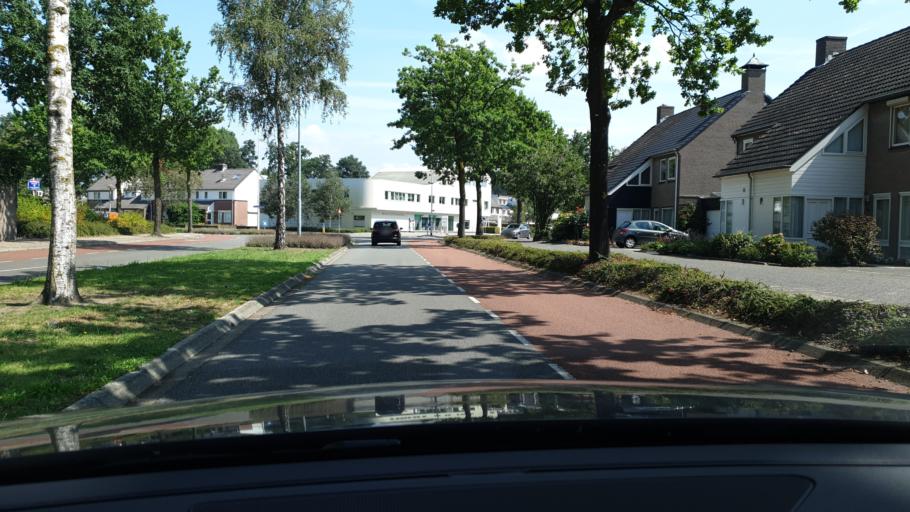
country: NL
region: North Brabant
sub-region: Gemeente Eindhoven
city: Eindhoven
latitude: 51.4823
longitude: 5.4498
